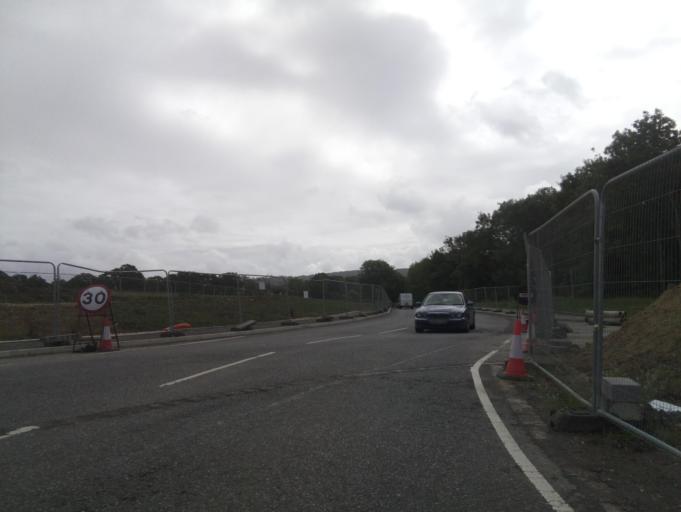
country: GB
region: England
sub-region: Hampshire
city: Fleet
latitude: 51.2461
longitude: -0.8539
